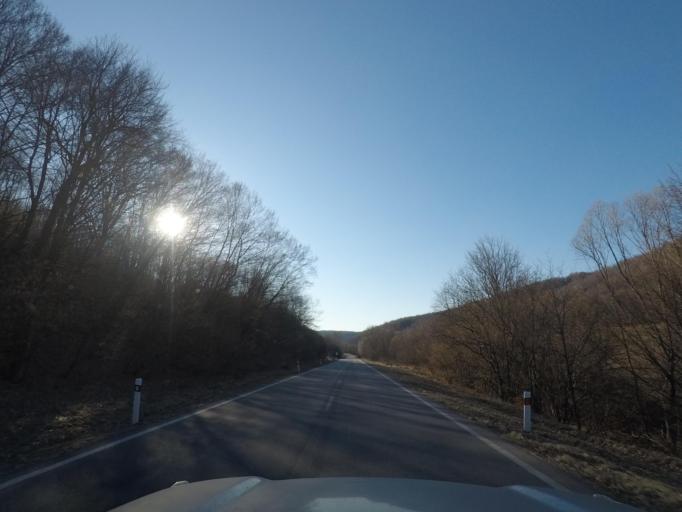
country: SK
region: Presovsky
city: Medzilaborce
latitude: 49.2807
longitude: 21.8378
